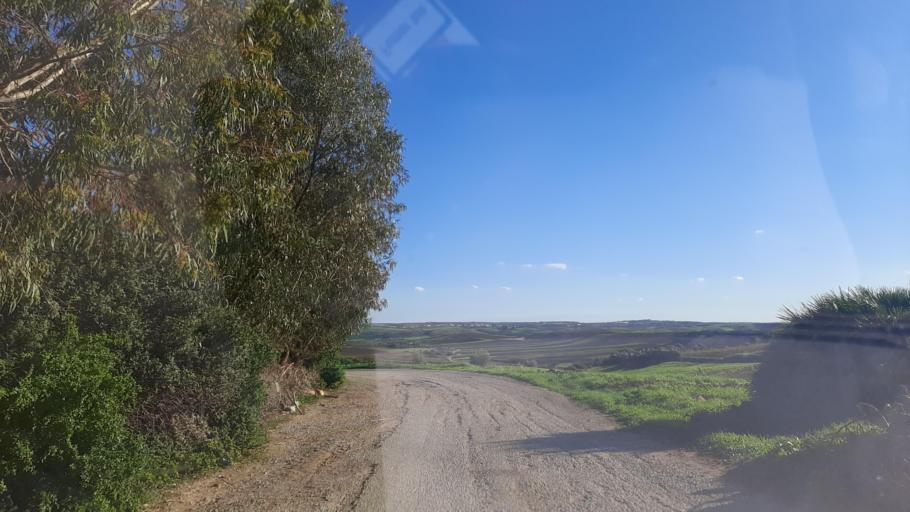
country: TN
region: Nabul
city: El Mida
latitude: 36.8384
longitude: 10.8292
